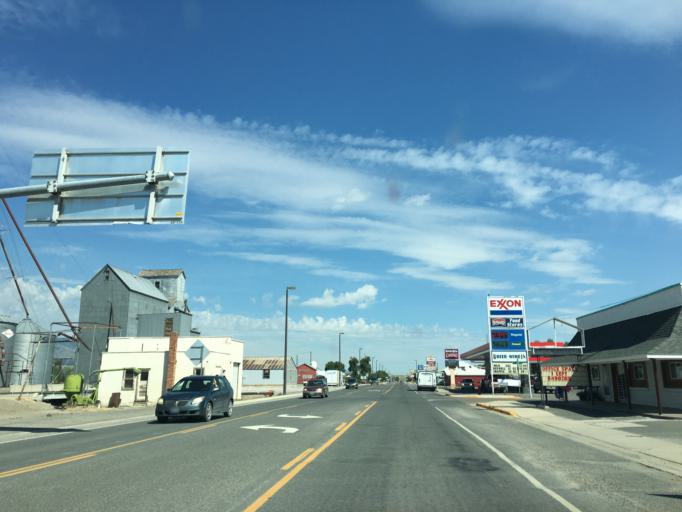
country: US
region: Montana
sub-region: Broadwater County
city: Townsend
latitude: 46.3199
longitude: -111.5218
